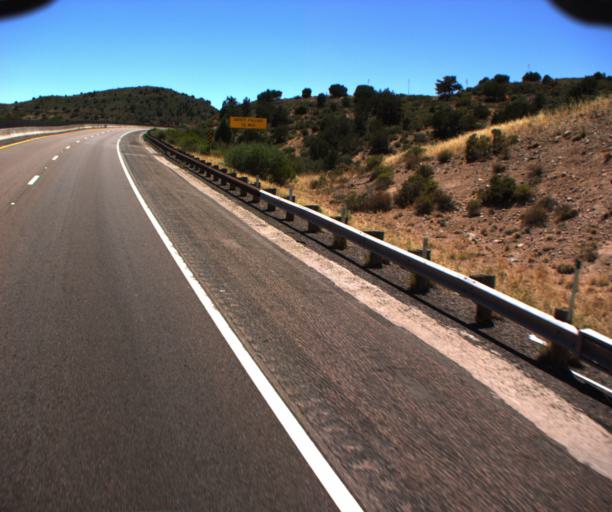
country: US
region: Arizona
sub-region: Gila County
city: Tonto Basin
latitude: 33.9291
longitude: -111.4437
